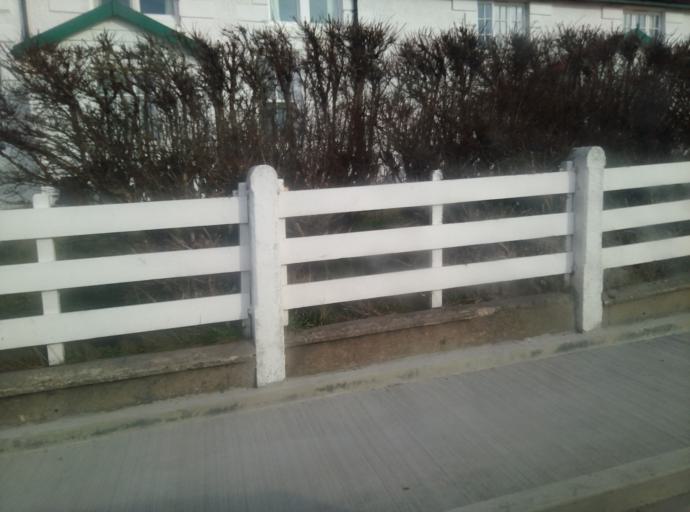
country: FK
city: Stanley
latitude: -51.6918
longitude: -57.8619
